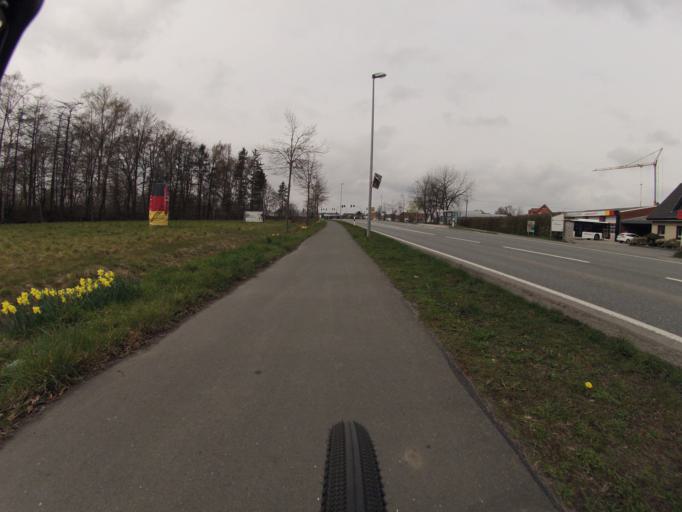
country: DE
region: North Rhine-Westphalia
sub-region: Regierungsbezirk Munster
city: Recke
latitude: 52.3593
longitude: 7.7199
